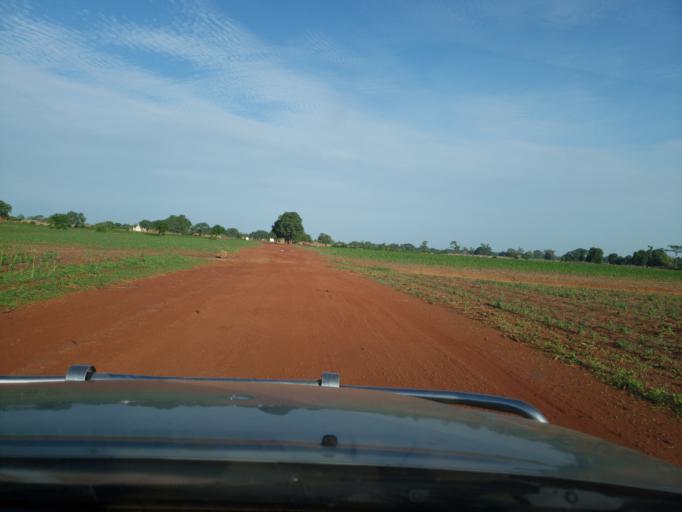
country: ML
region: Sikasso
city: Koutiala
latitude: 12.4295
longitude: -5.6065
